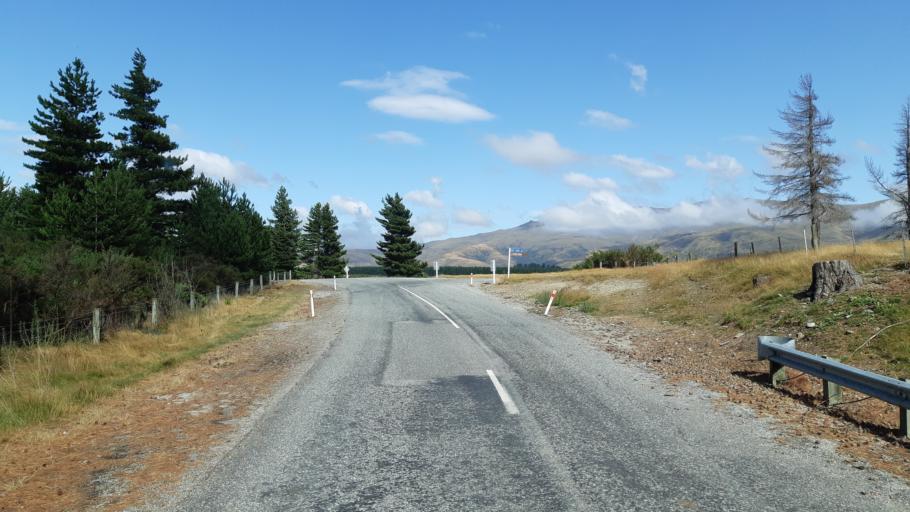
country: NZ
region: Otago
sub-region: Queenstown-Lakes District
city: Wanaka
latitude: -44.8692
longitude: 169.7992
